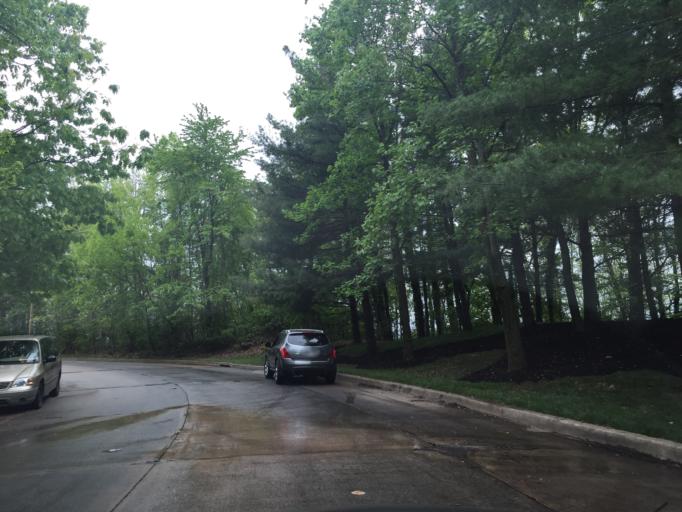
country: US
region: Maryland
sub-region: Baltimore County
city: Lochearn
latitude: 39.3468
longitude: -76.6581
